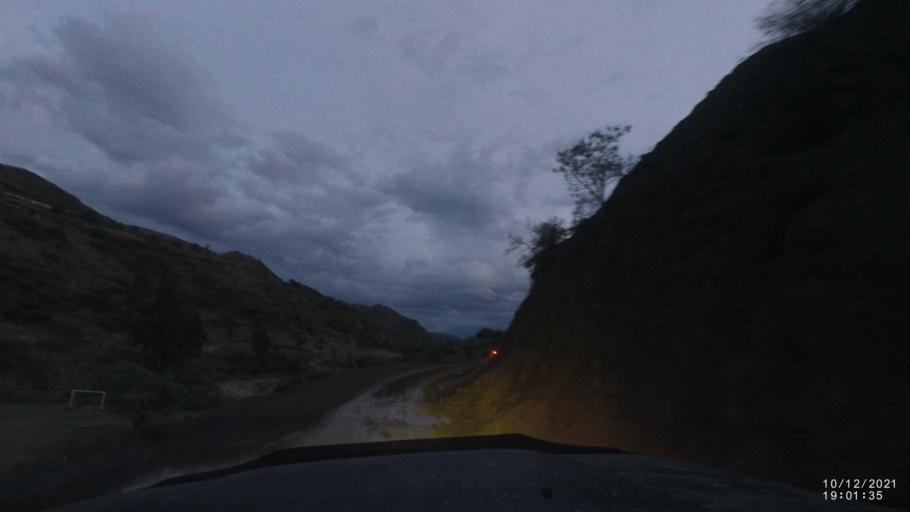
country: BO
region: Cochabamba
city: Tarata
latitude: -17.8976
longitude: -65.9461
